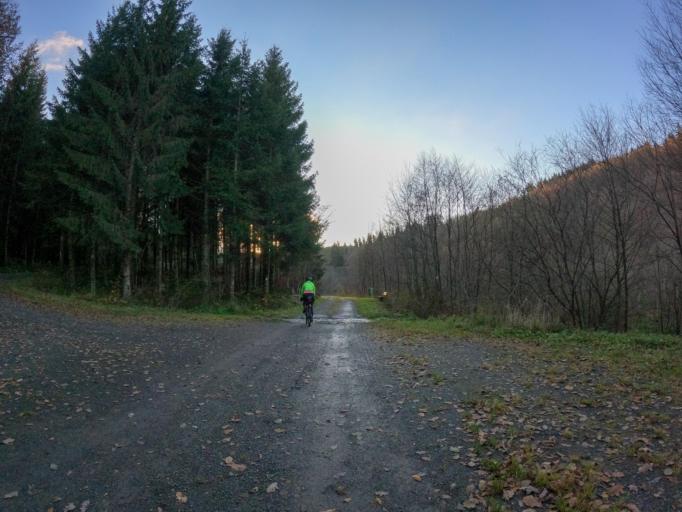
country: LU
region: Diekirch
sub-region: Canton de Wiltz
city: Bavigne
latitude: 49.9472
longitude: 5.8372
